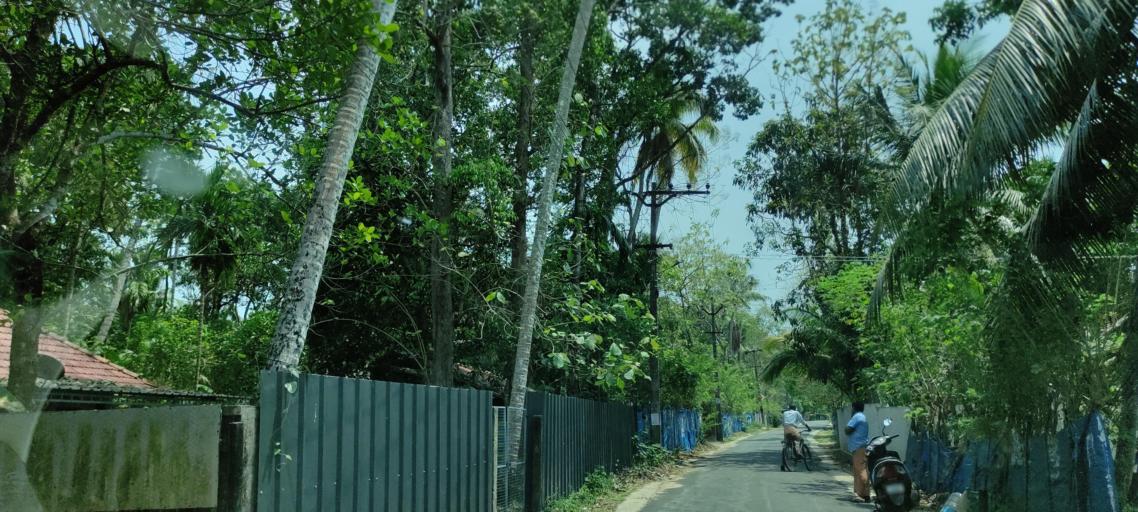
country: IN
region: Kerala
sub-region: Alappuzha
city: Vayalar
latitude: 9.7206
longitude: 76.3408
